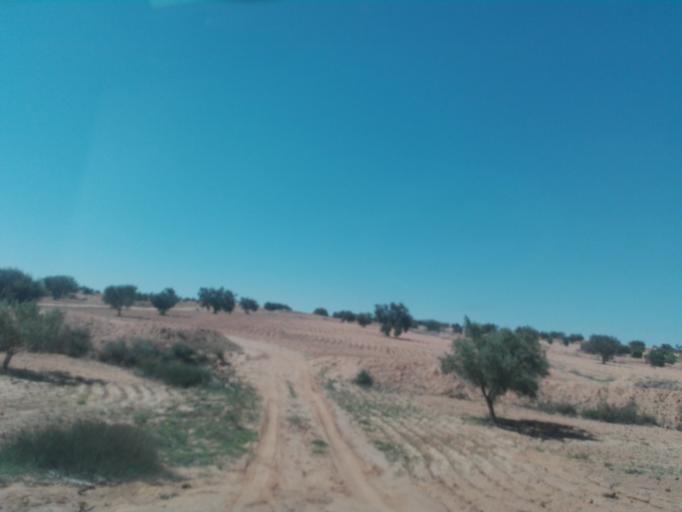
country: TN
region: Safaqis
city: Bi'r `Ali Bin Khalifah
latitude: 34.7974
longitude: 10.2845
